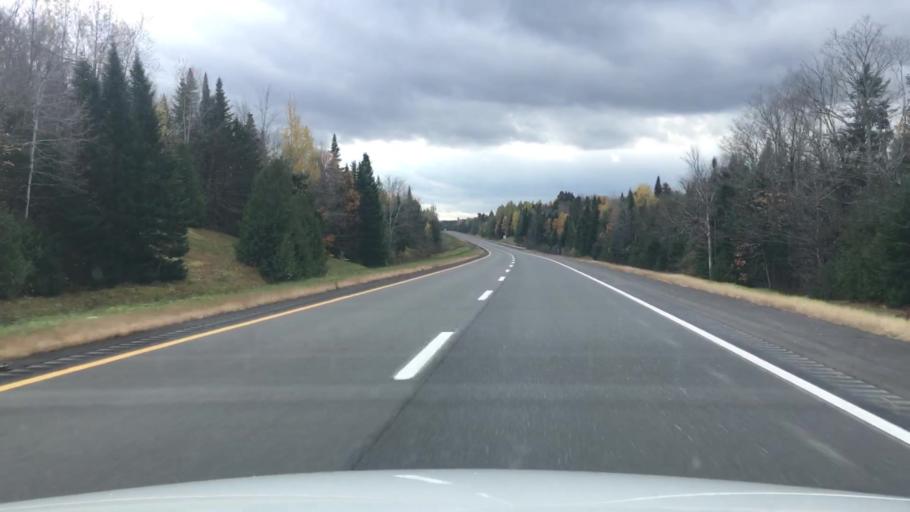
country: US
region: Maine
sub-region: Penobscot County
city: Patten
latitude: 46.0875
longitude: -68.2069
